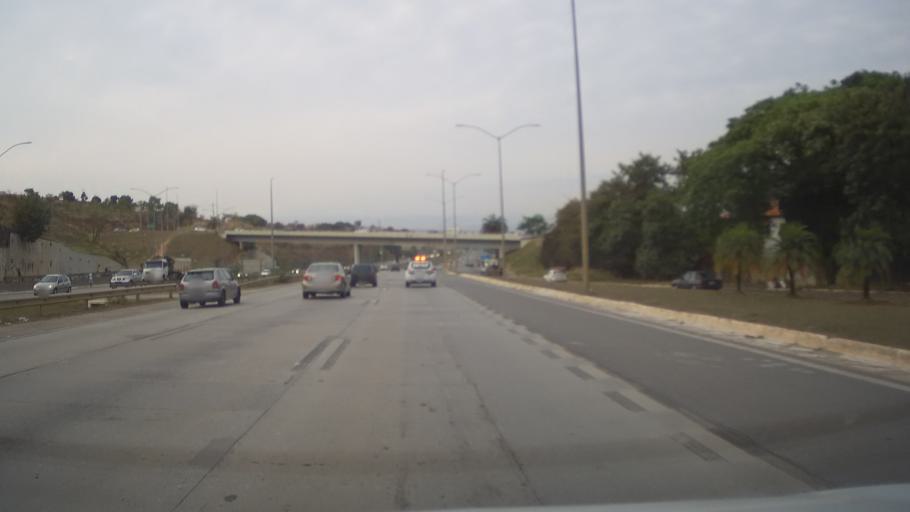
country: BR
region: Minas Gerais
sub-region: Vespasiano
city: Vespasiano
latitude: -19.7780
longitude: -43.9488
